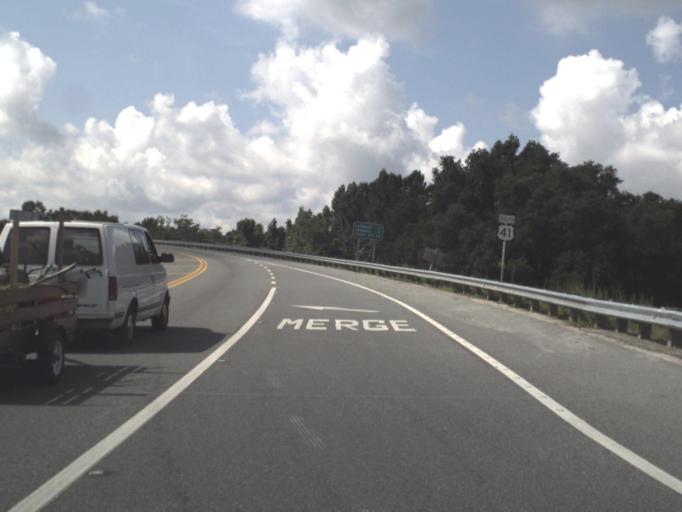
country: US
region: Florida
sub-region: Marion County
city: Dunnellon
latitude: 29.0430
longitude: -82.4669
